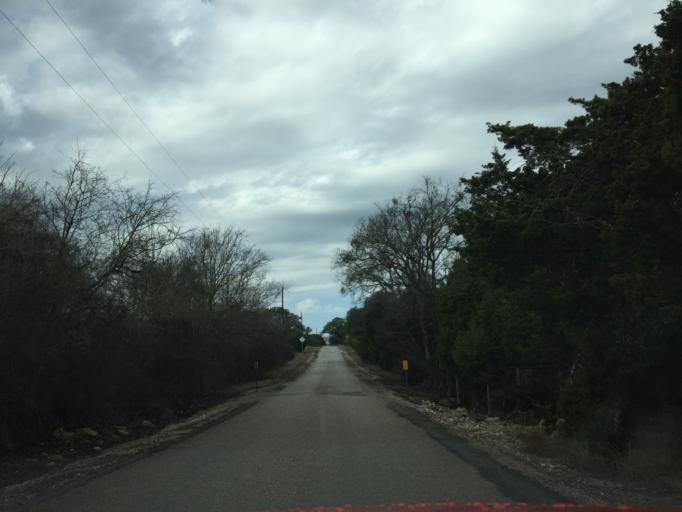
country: US
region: Texas
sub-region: Burnet County
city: Bertram
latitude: 30.6317
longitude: -98.0001
